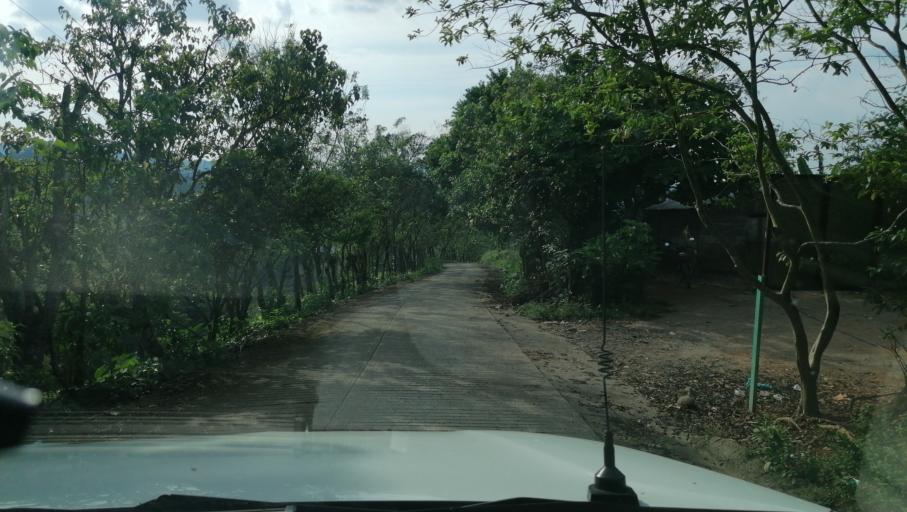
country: MX
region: Chiapas
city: Pichucalco
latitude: 17.4827
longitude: -93.2270
